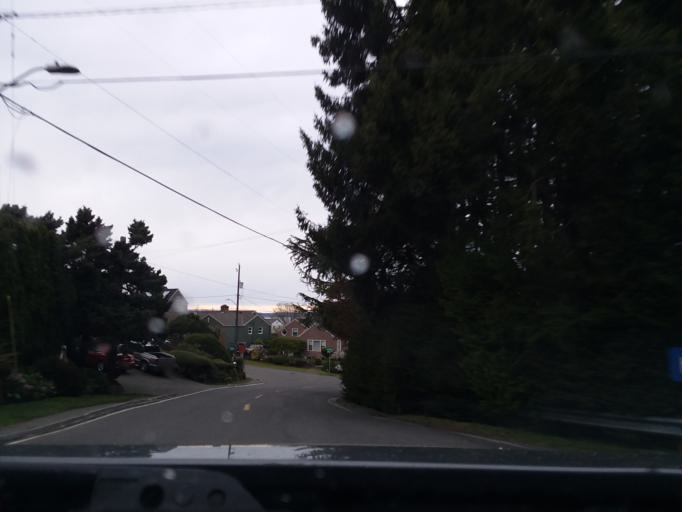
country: US
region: Washington
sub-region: King County
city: Shoreline
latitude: 47.6979
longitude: -122.3933
